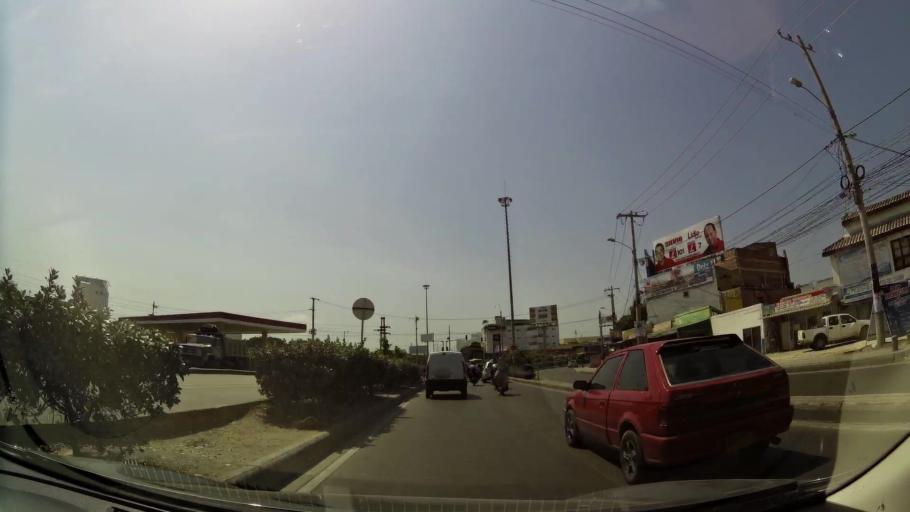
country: CO
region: Bolivar
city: Cartagena
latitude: 10.3936
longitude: -75.4822
